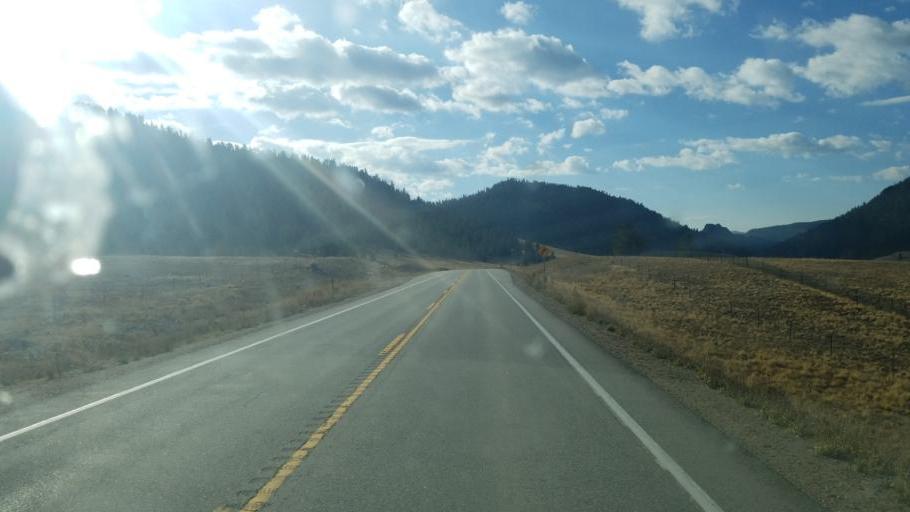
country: US
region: Colorado
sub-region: Chaffee County
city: Buena Vista
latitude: 38.8763
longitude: -105.9859
